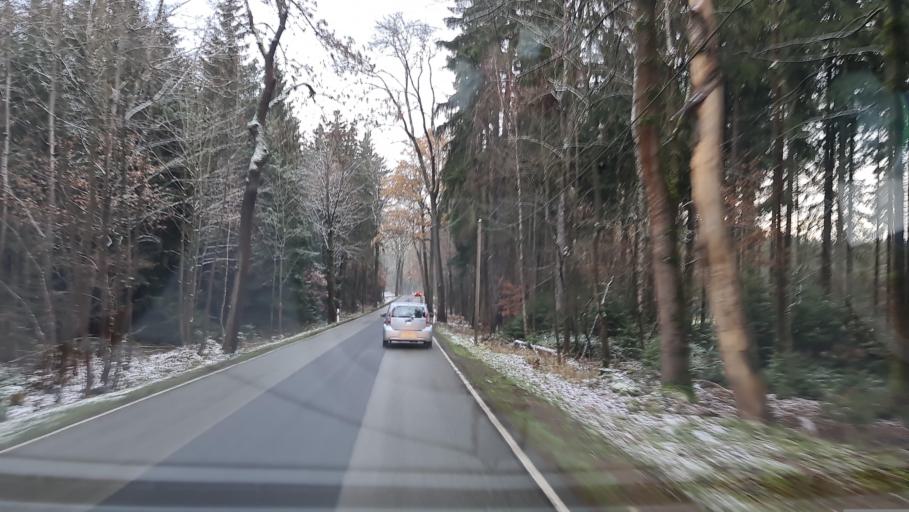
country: DE
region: Saxony
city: Limbach
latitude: 50.5909
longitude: 12.2787
